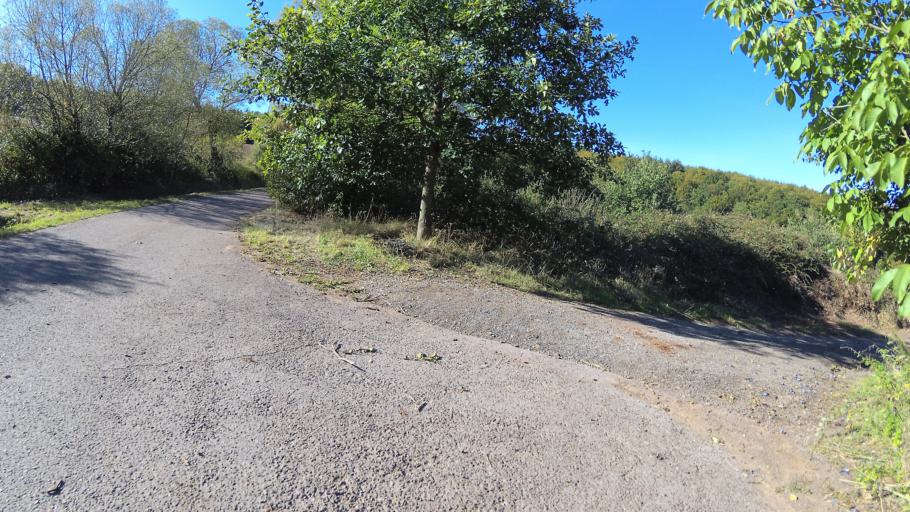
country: DE
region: Saarland
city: Eppelborn
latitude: 49.4255
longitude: 6.9936
